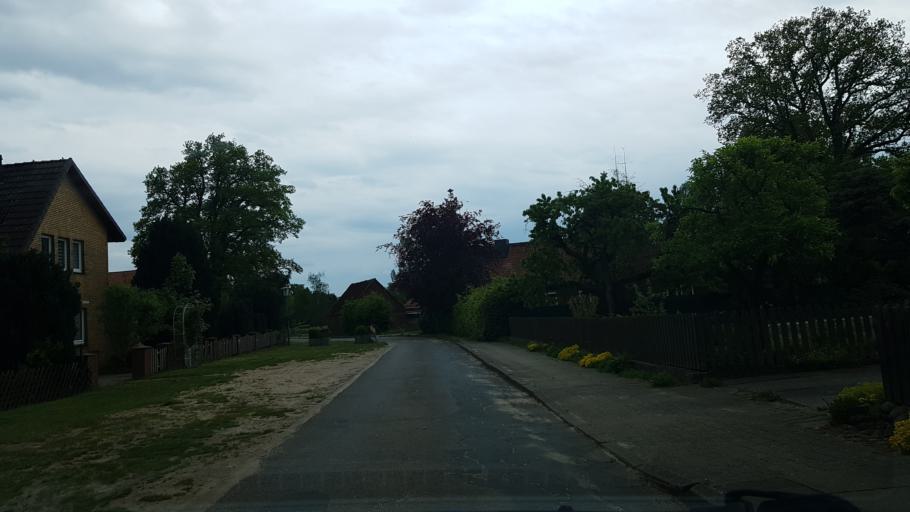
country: DE
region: Lower Saxony
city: Vastorf
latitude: 53.2089
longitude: 10.5426
